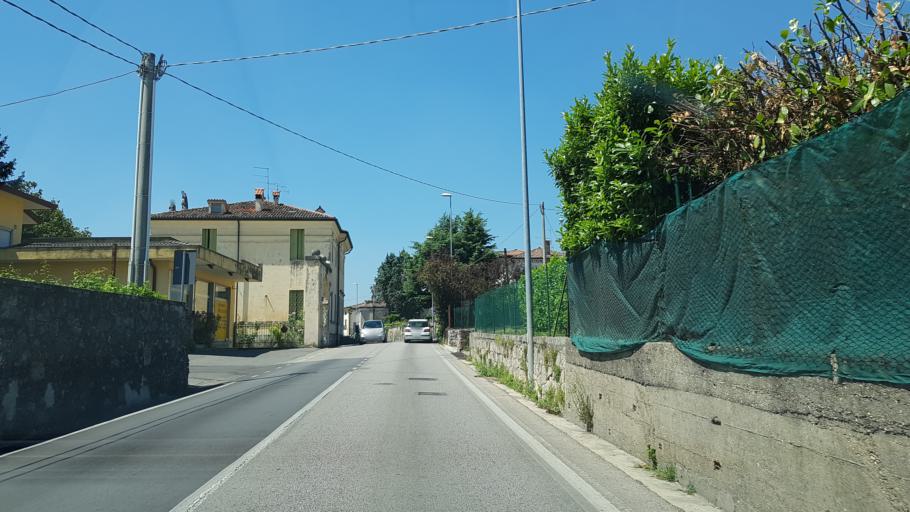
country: IT
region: Veneto
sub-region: Provincia di Vicenza
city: Creazzo
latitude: 45.5333
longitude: 11.4714
